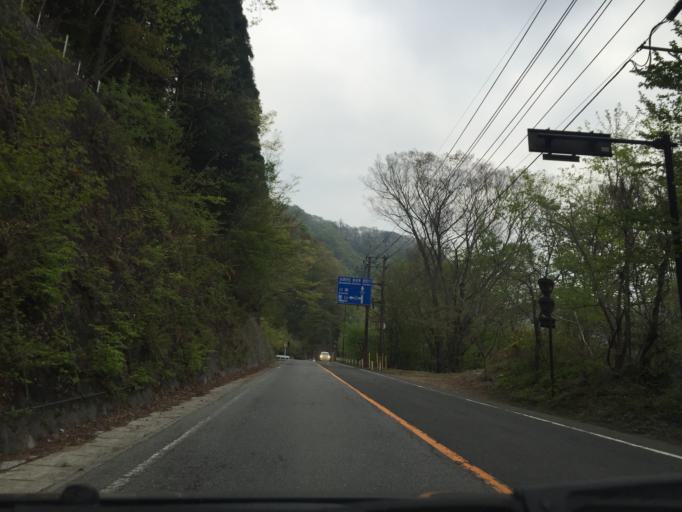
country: JP
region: Tochigi
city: Nikko
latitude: 36.9064
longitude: 139.7021
